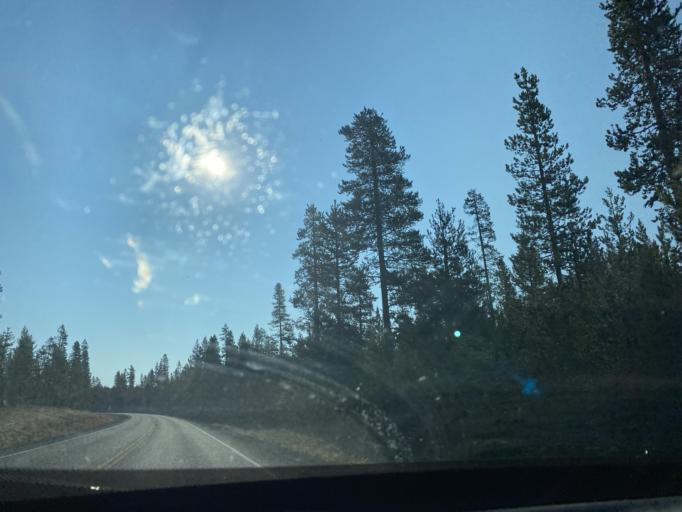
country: US
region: Oregon
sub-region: Deschutes County
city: Three Rivers
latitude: 43.7058
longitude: -121.2931
